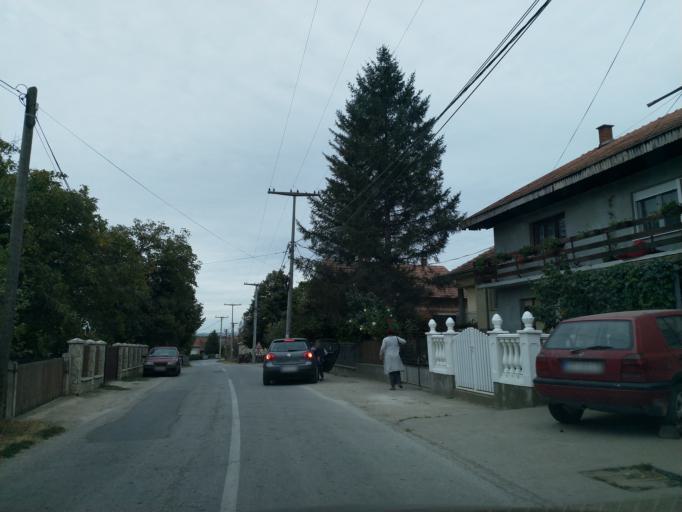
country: RS
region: Central Serbia
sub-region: Pomoravski Okrug
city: Paracin
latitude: 43.8382
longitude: 21.3204
